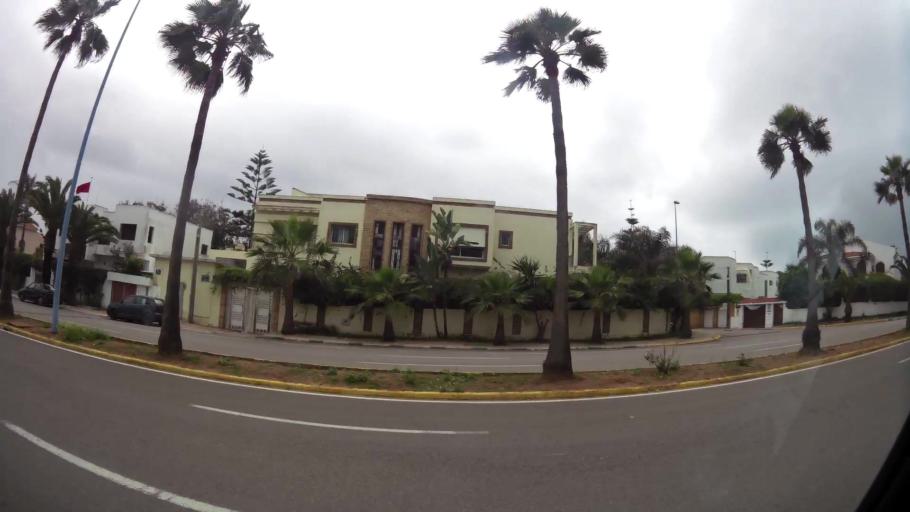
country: MA
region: Grand Casablanca
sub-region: Casablanca
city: Casablanca
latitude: 33.6033
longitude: -7.6546
